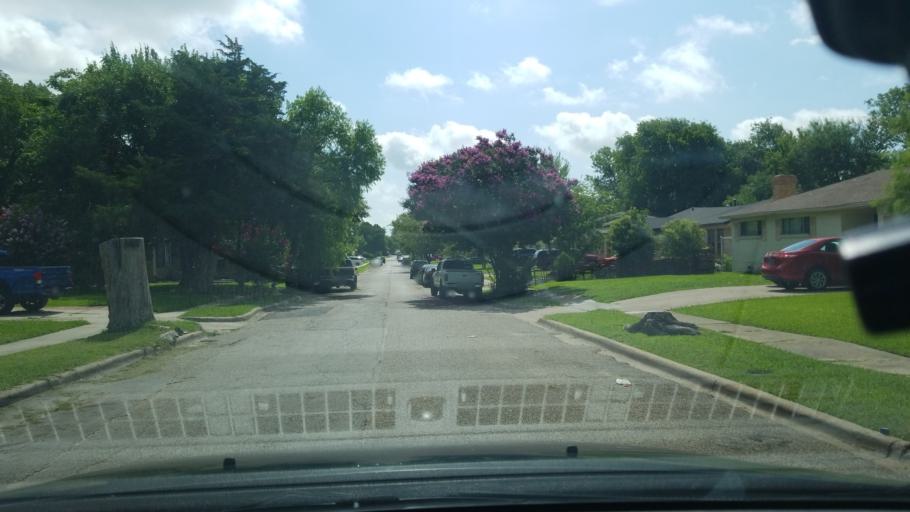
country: US
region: Texas
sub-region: Dallas County
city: Mesquite
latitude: 32.8172
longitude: -96.6529
